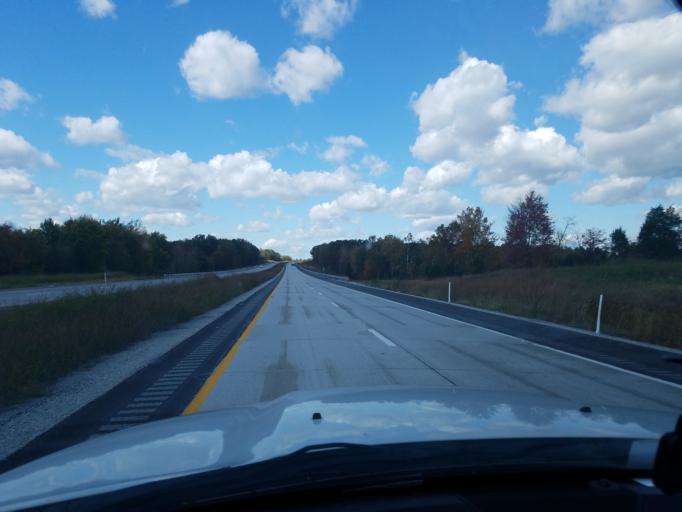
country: US
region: Kentucky
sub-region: Ohio County
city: Oak Grove
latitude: 37.3451
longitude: -86.7749
